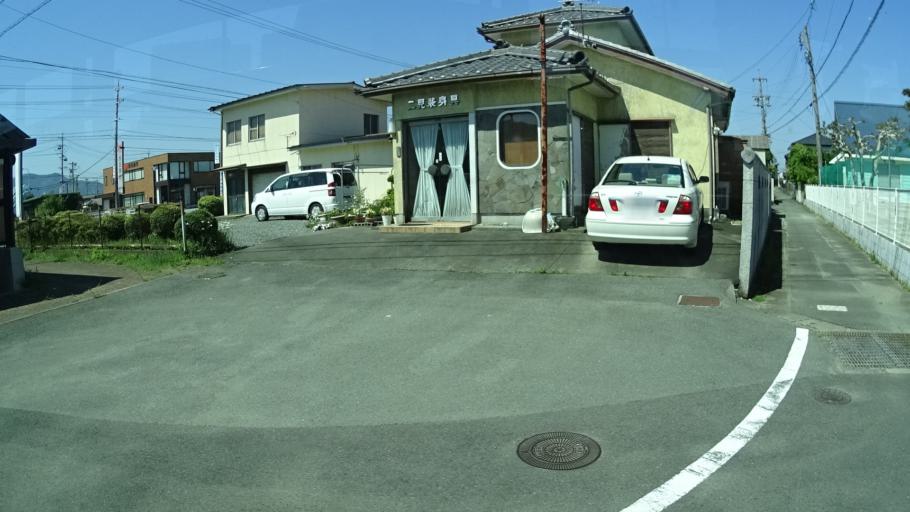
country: JP
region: Mie
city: Toba
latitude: 34.5051
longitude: 136.7759
